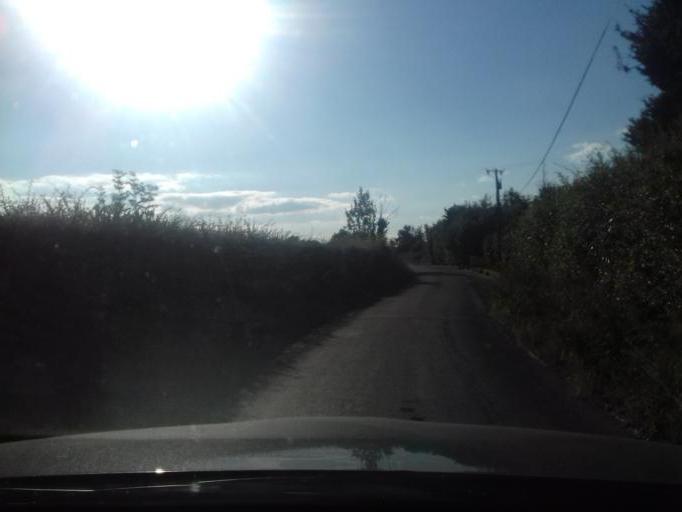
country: IE
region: Leinster
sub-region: An Mhi
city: Ashbourne
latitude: 53.4541
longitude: -6.3807
